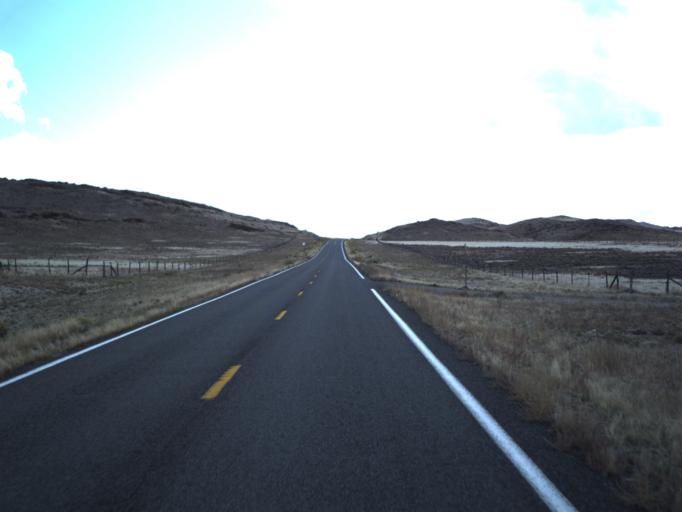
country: US
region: Utah
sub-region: Beaver County
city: Milford
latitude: 38.6320
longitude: -113.8549
